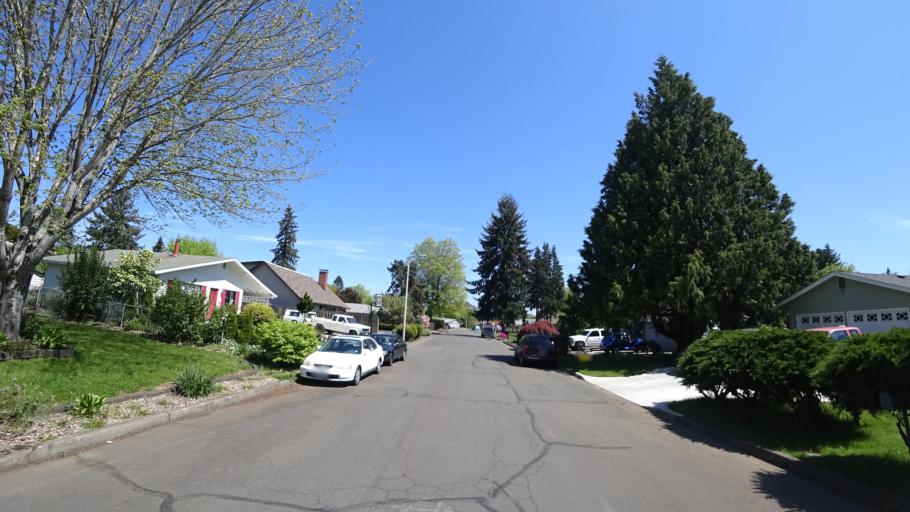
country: US
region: Oregon
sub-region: Washington County
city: Hillsboro
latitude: 45.5106
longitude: -122.9648
